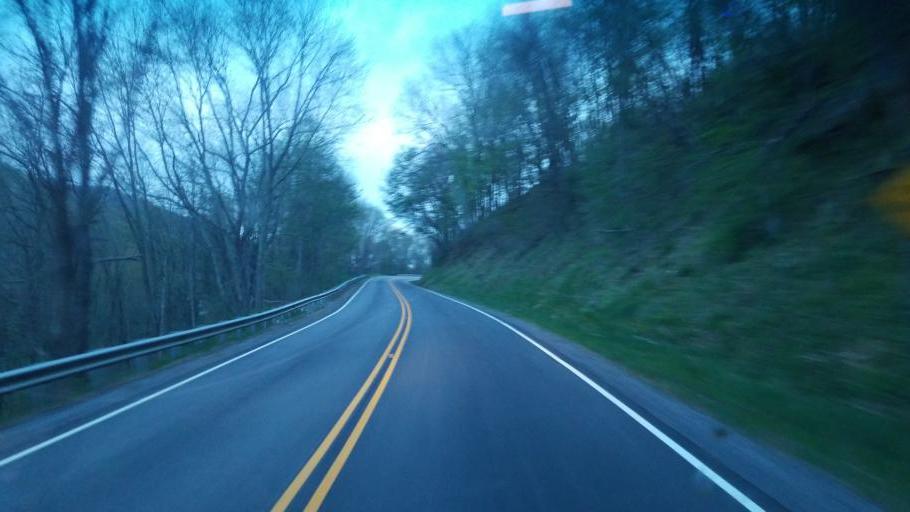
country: US
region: Virginia
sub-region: Smyth County
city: Atkins
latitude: 36.8174
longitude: -81.4418
